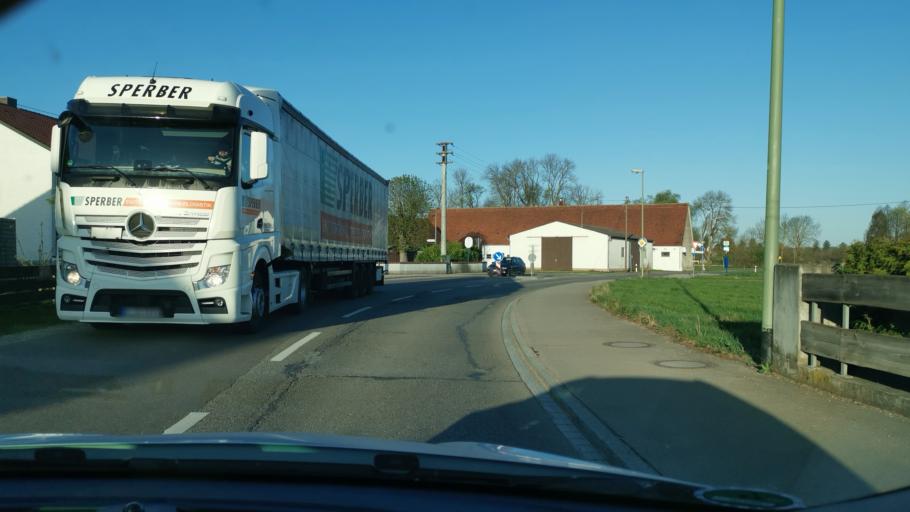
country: DE
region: Bavaria
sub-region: Swabia
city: Rehling
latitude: 48.4884
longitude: 10.8934
